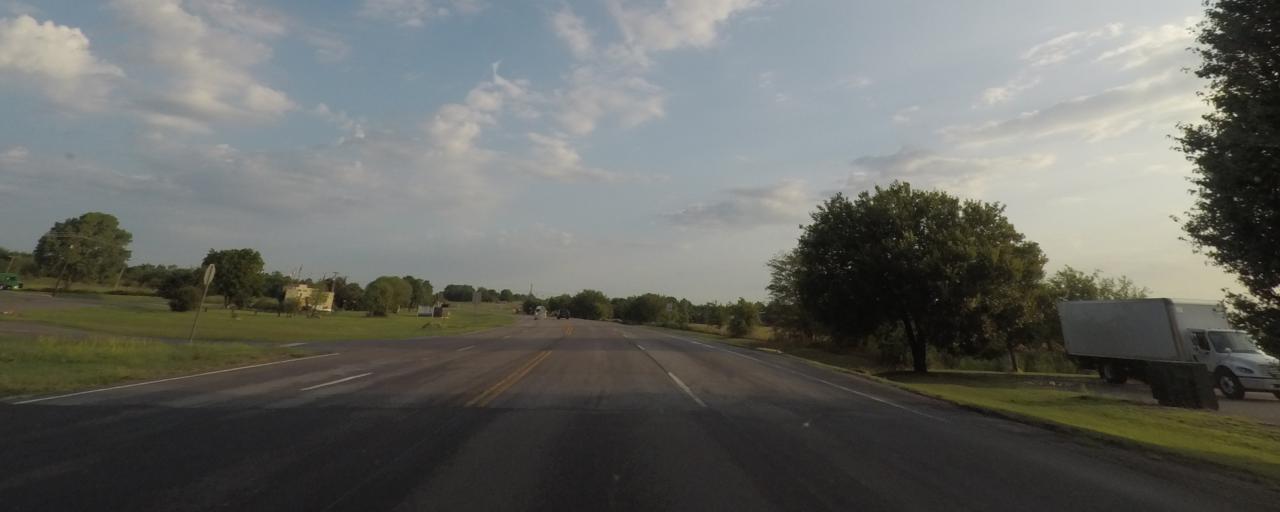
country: US
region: Oklahoma
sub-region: Stephens County
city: Comanche
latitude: 34.3732
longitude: -97.9642
